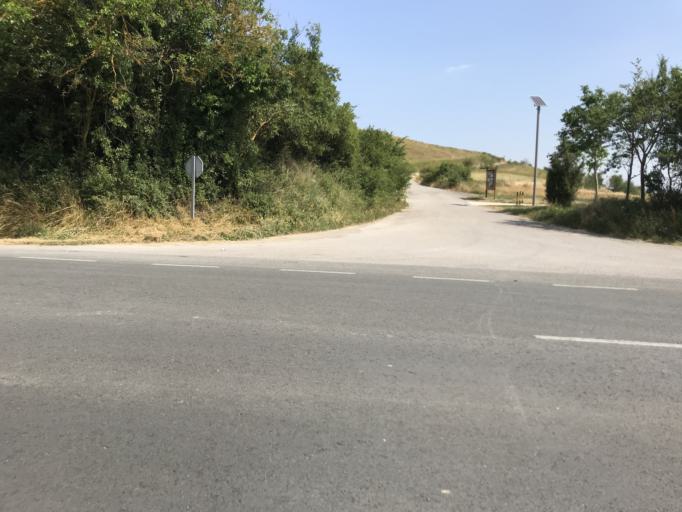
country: ES
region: Basque Country
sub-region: Provincia de Alava
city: Gasteiz / Vitoria
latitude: 42.8285
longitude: -2.6505
